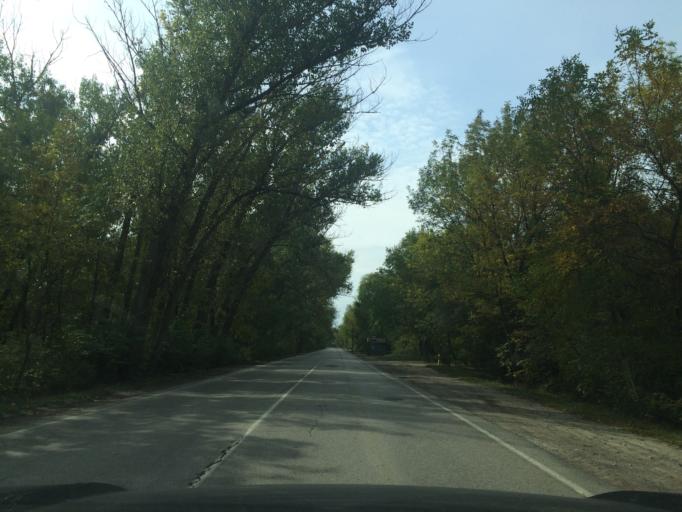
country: RU
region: Rostov
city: Kalinin
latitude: 47.1765
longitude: 39.5690
